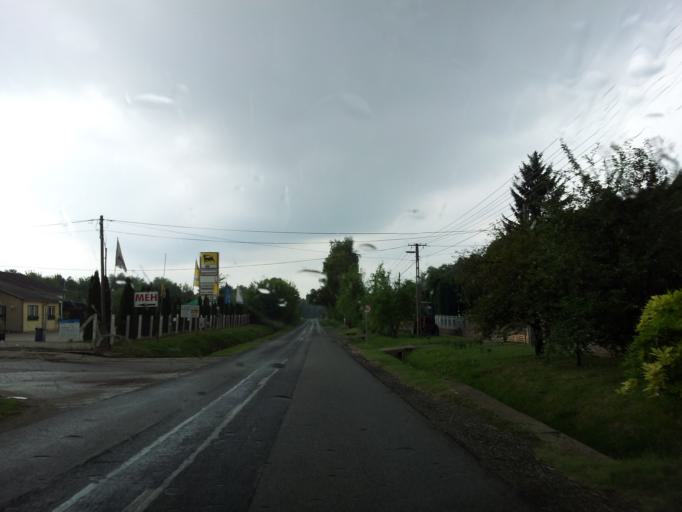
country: HU
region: Tolna
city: Hogyesz
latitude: 46.5059
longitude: 18.4106
